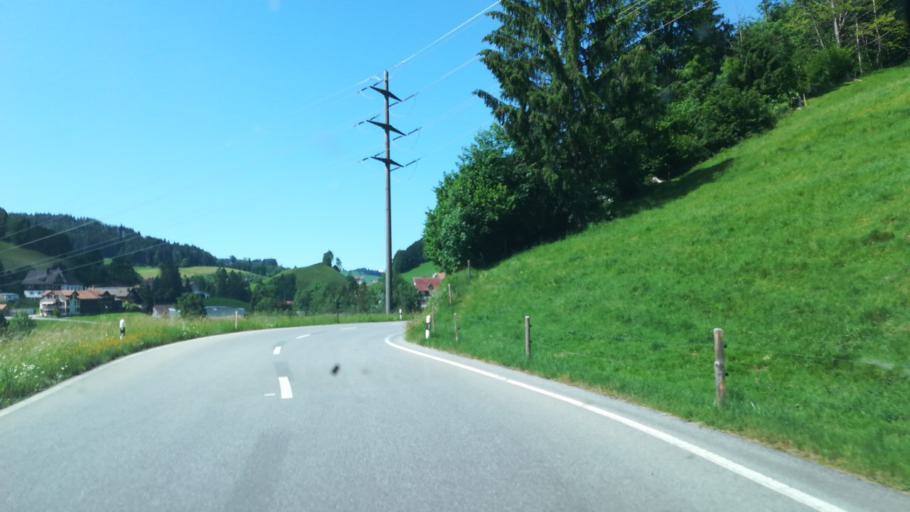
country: CH
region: Appenzell Ausserrhoden
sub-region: Bezirk Hinterland
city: Urnasch
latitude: 47.3248
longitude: 9.2967
